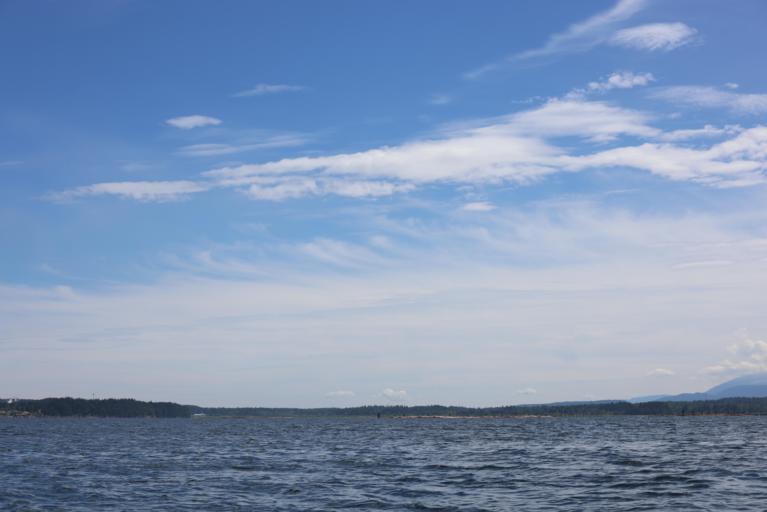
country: CA
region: British Columbia
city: Nanaimo
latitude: 49.1653
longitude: -123.9206
